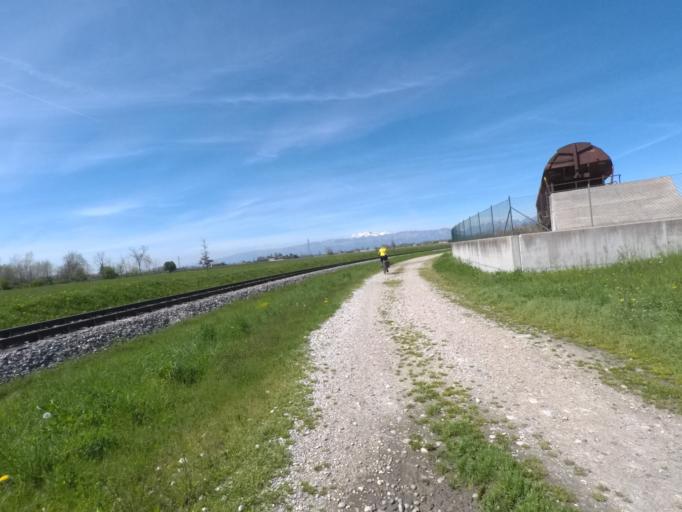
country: IT
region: Friuli Venezia Giulia
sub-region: Provincia di Pordenone
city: Rosa
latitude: 45.9526
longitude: 12.8809
